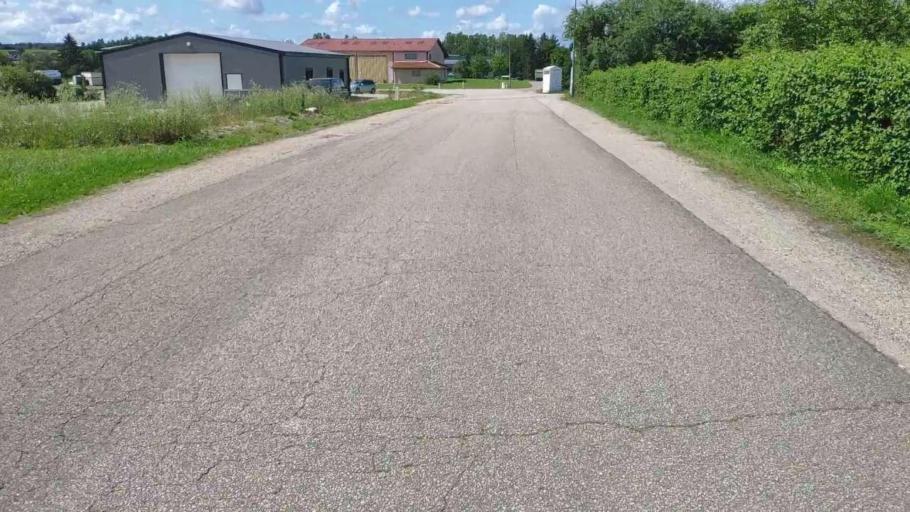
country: FR
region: Franche-Comte
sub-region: Departement du Jura
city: Bletterans
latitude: 46.8327
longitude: 5.5581
